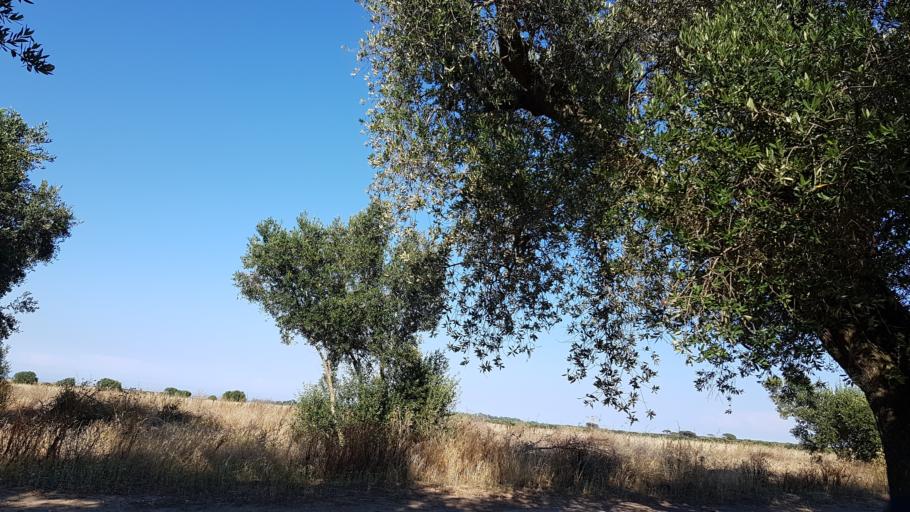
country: IT
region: Apulia
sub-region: Provincia di Brindisi
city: La Rosa
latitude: 40.5918
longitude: 17.9917
